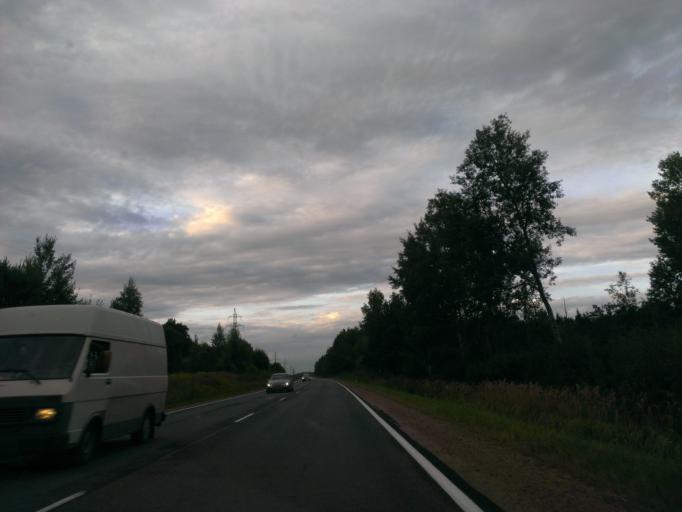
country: LV
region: Salaspils
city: Salaspils
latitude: 56.8667
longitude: 24.4068
